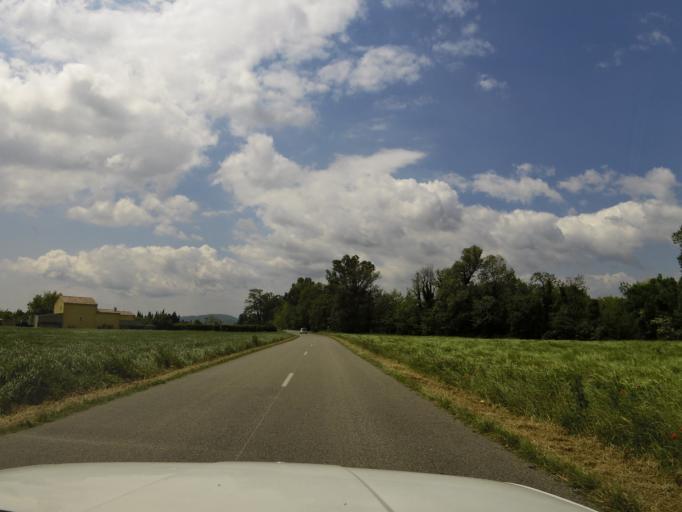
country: FR
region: Rhone-Alpes
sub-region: Departement de la Drome
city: Ancone
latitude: 44.5898
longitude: 4.7433
